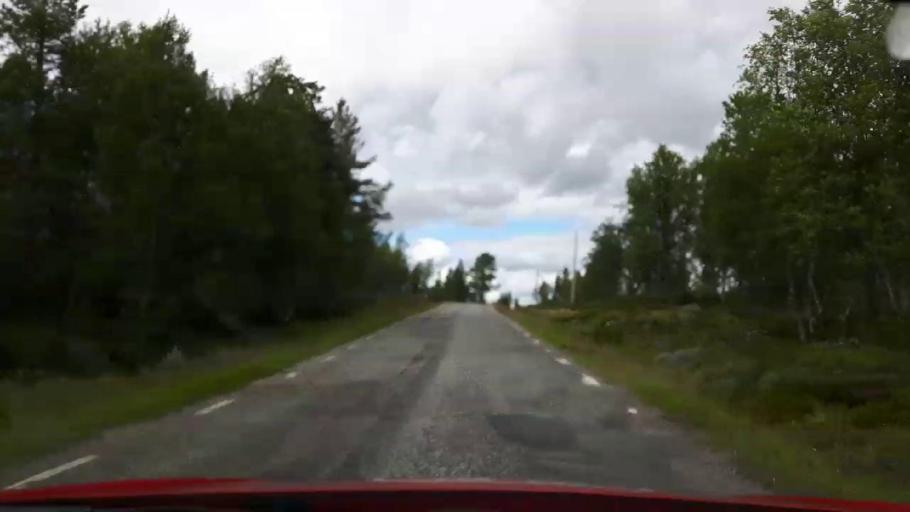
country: NO
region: Hedmark
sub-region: Engerdal
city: Engerdal
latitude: 62.3248
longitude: 12.8086
